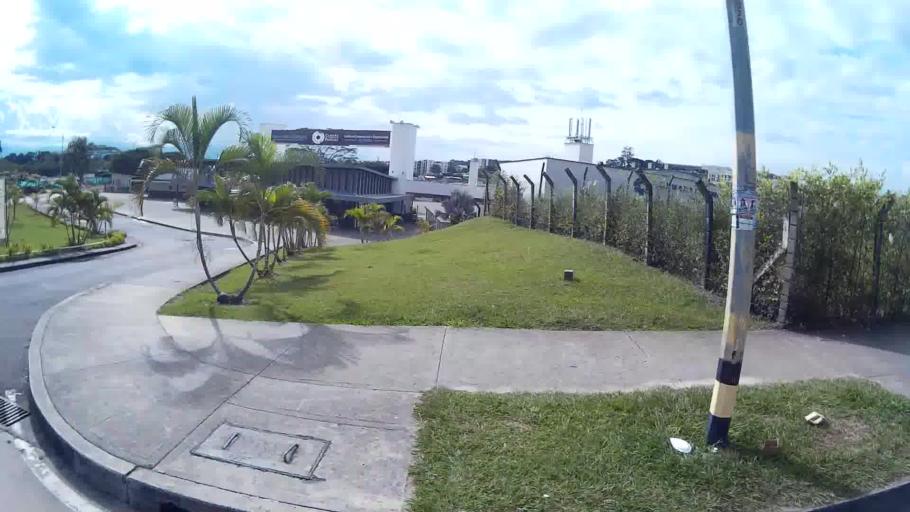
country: CO
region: Risaralda
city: Pereira
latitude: 4.8050
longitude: -75.7554
